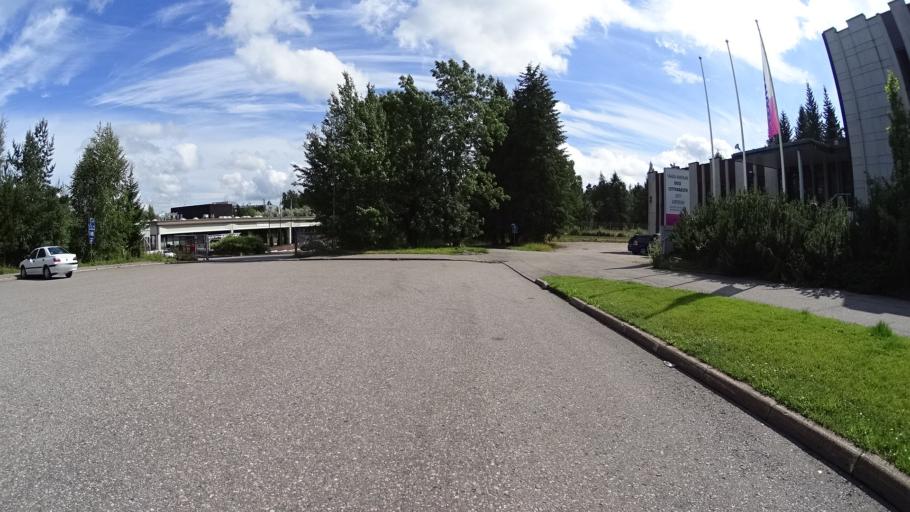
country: FI
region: Uusimaa
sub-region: Helsinki
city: Kilo
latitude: 60.2077
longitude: 24.7590
